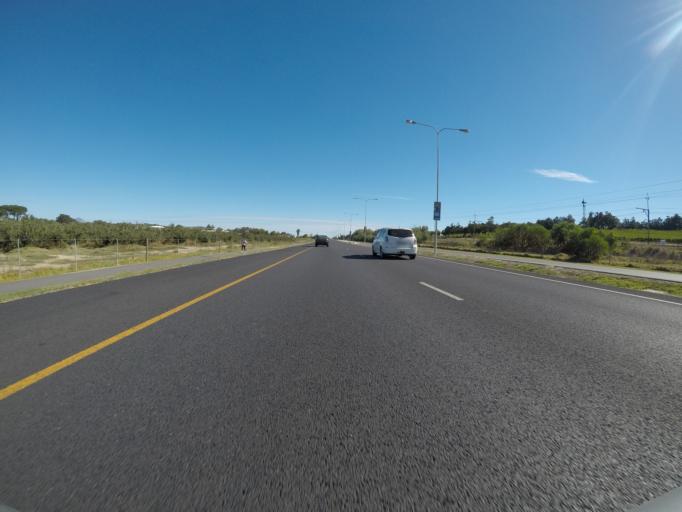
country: ZA
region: Western Cape
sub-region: Cape Winelands District Municipality
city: Stellenbosch
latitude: -33.9867
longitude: 18.7679
